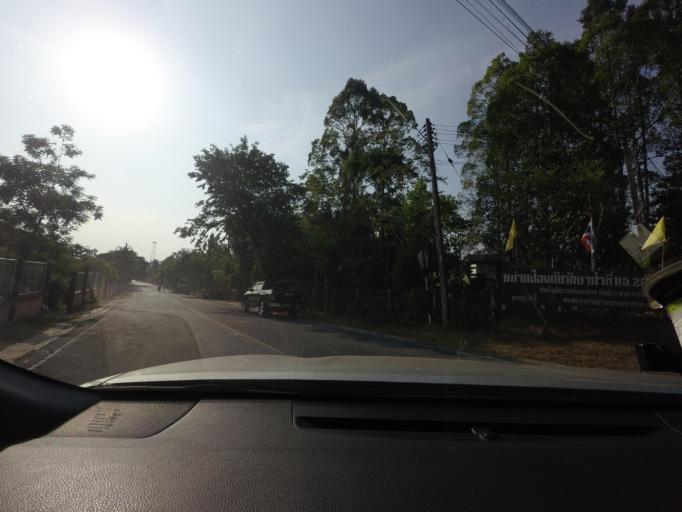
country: TH
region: Narathiwat
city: Rueso
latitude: 6.4002
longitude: 101.5253
